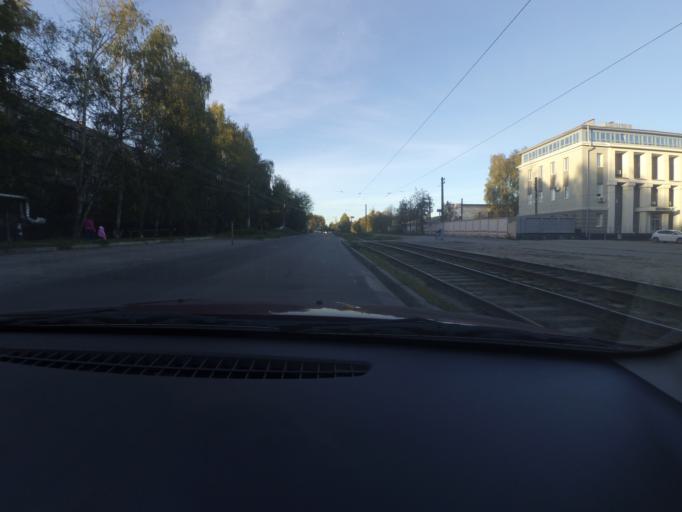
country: RU
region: Nizjnij Novgorod
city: Nizhniy Novgorod
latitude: 56.2823
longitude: 43.9932
